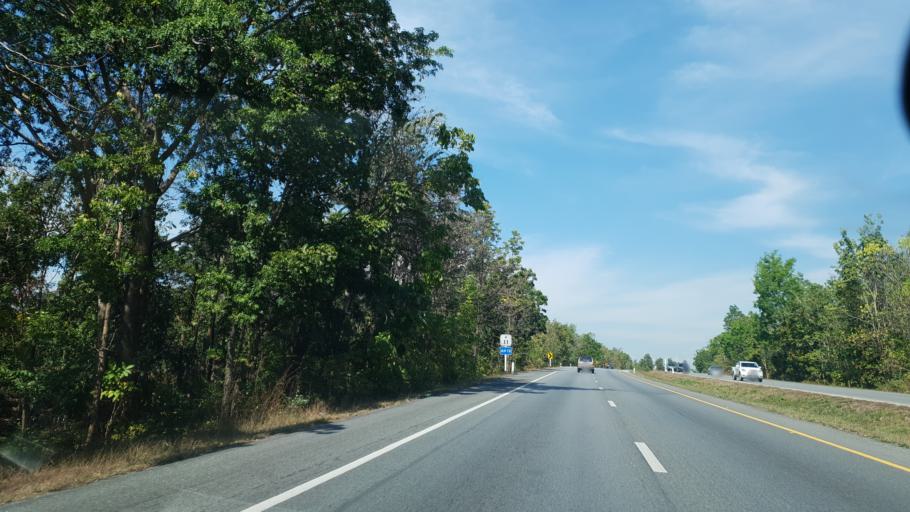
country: TH
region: Uttaradit
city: Thong Saen Khan
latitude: 17.4206
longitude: 100.2263
